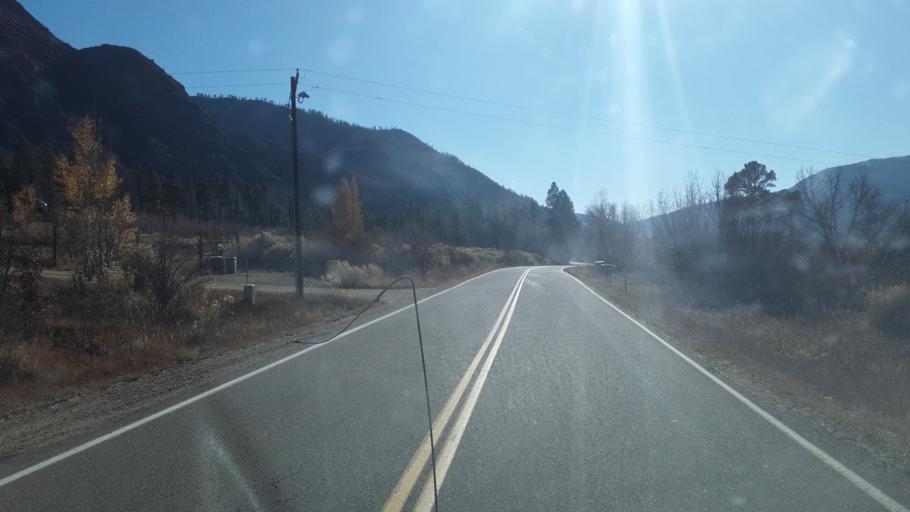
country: US
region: Colorado
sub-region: La Plata County
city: Durango
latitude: 37.4067
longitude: -107.8140
